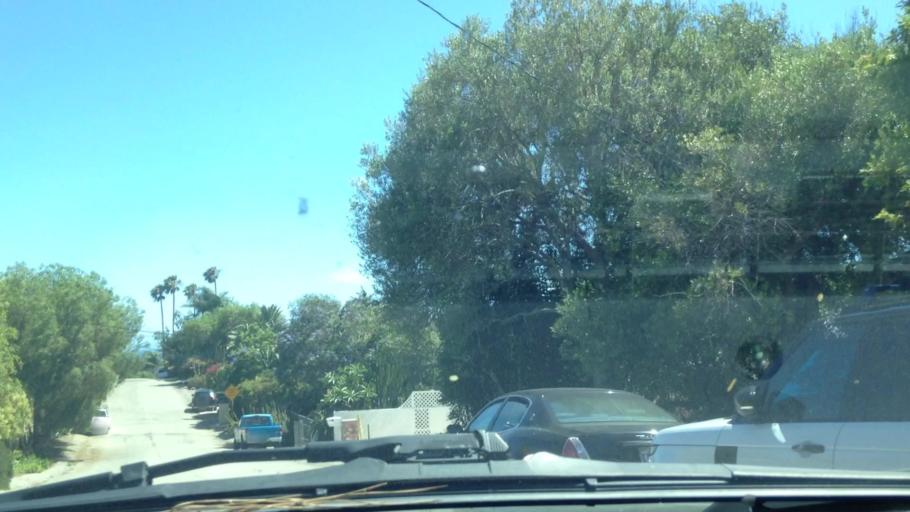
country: US
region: California
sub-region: Los Angeles County
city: Malibu
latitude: 34.0185
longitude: -118.8038
